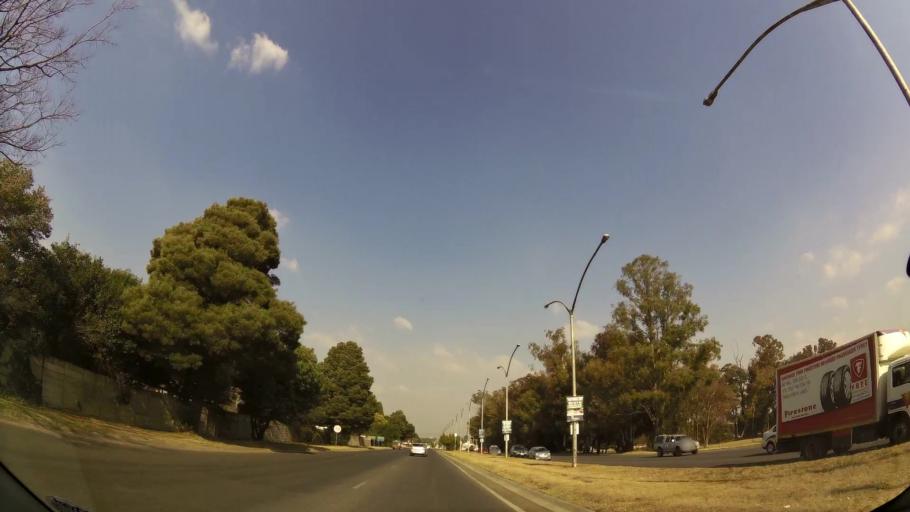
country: ZA
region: Gauteng
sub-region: Ekurhuleni Metropolitan Municipality
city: Benoni
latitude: -26.1368
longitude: 28.2931
